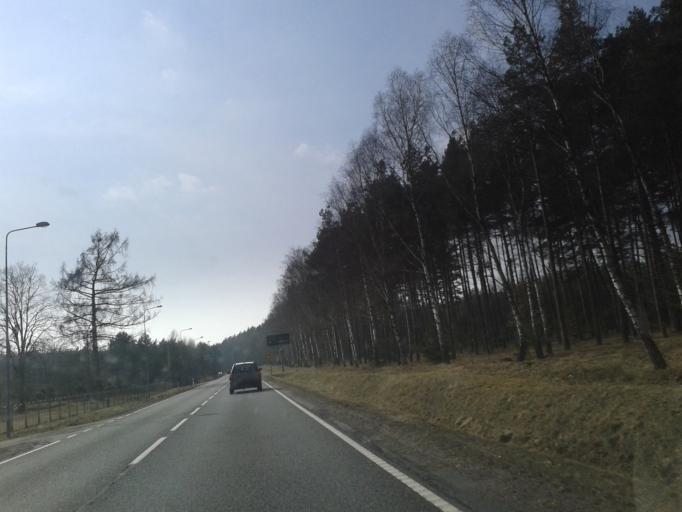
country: PL
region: Pomeranian Voivodeship
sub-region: Powiat czluchowski
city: Czarne
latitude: 53.5609
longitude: 17.0331
